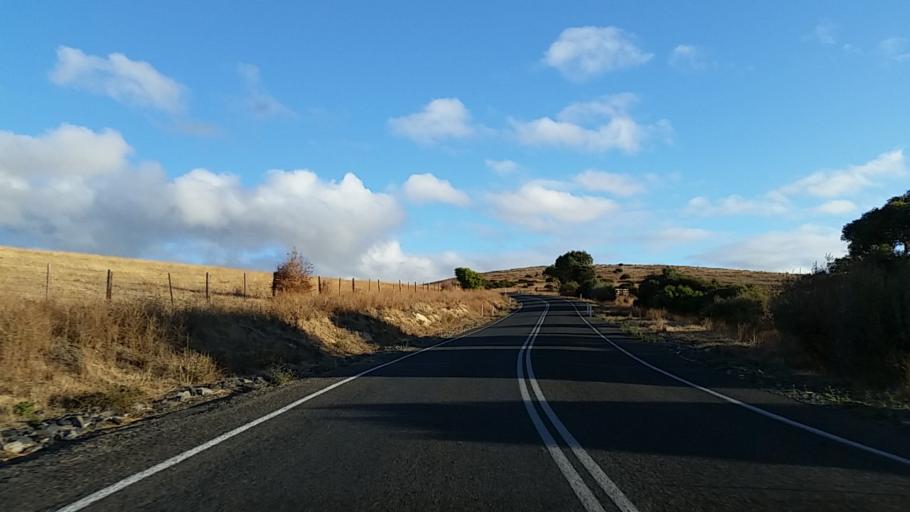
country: AU
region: South Australia
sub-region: Yankalilla
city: Normanville
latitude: -35.5371
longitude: 138.1943
